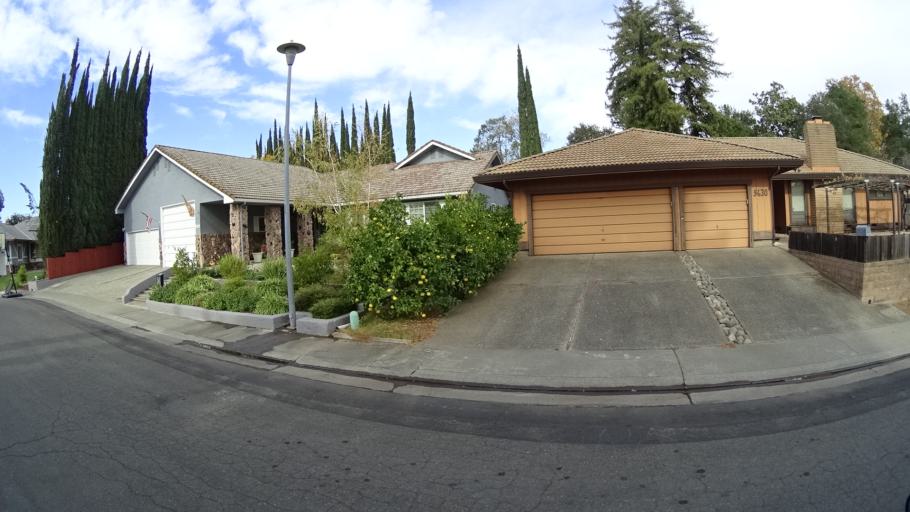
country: US
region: California
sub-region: Sacramento County
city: Fair Oaks
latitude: 38.6695
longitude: -121.2631
